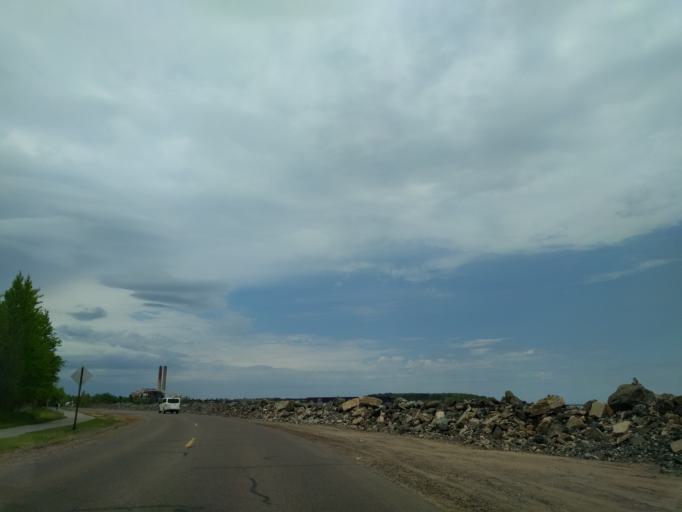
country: US
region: Michigan
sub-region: Marquette County
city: Marquette
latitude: 46.5634
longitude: -87.3893
